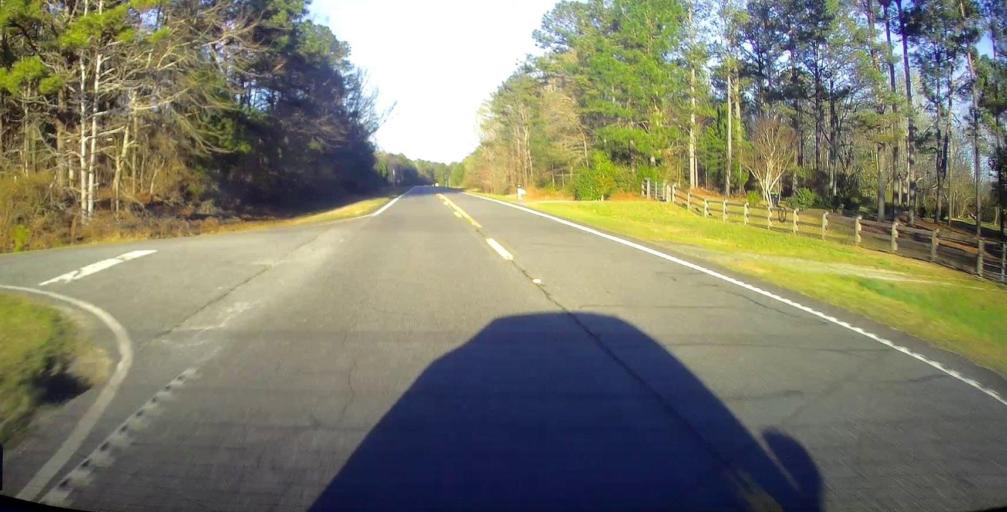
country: US
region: Georgia
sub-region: Talbot County
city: Talbotton
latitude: 32.6580
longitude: -84.6600
